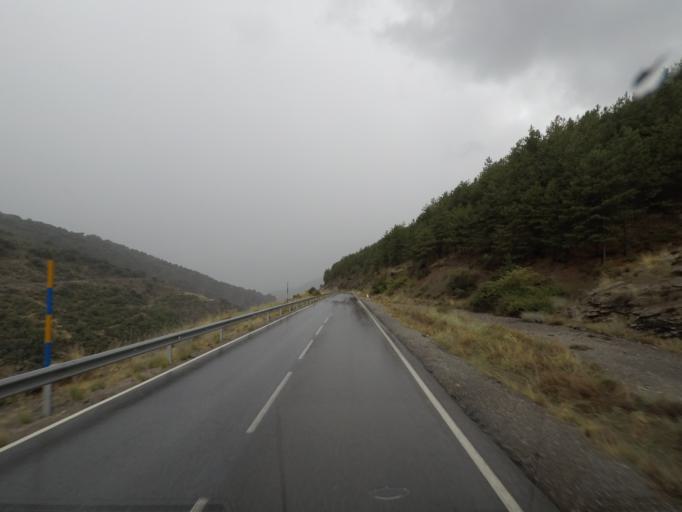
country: ES
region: Andalusia
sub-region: Provincia de Almeria
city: Bayarcal
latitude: 37.0698
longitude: -3.0175
